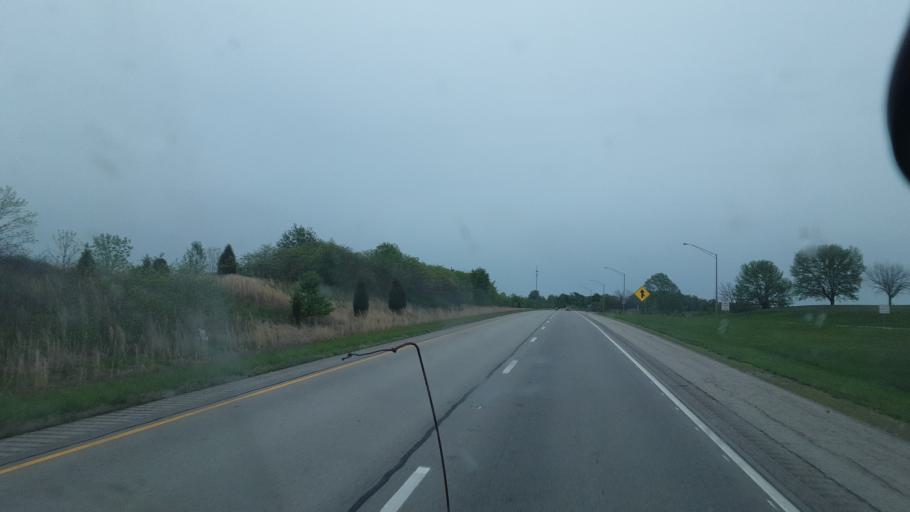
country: US
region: Indiana
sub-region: Spencer County
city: Dale
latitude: 38.1955
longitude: -86.9480
